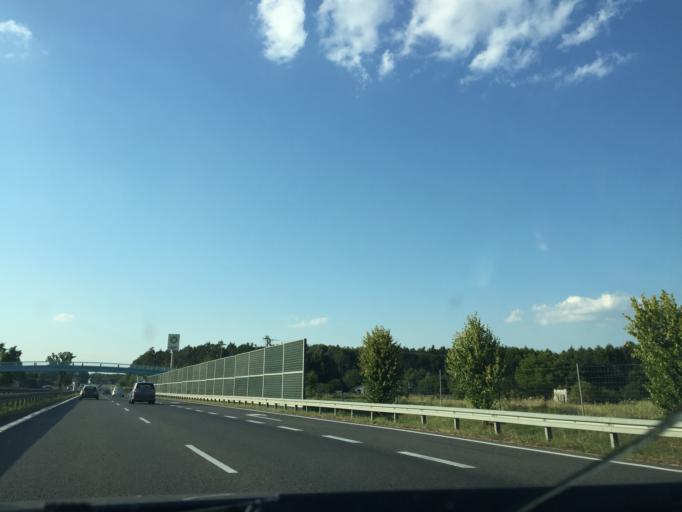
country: PL
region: Masovian Voivodeship
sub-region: Powiat bialobrzeski
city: Sucha
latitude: 51.6204
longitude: 20.9747
